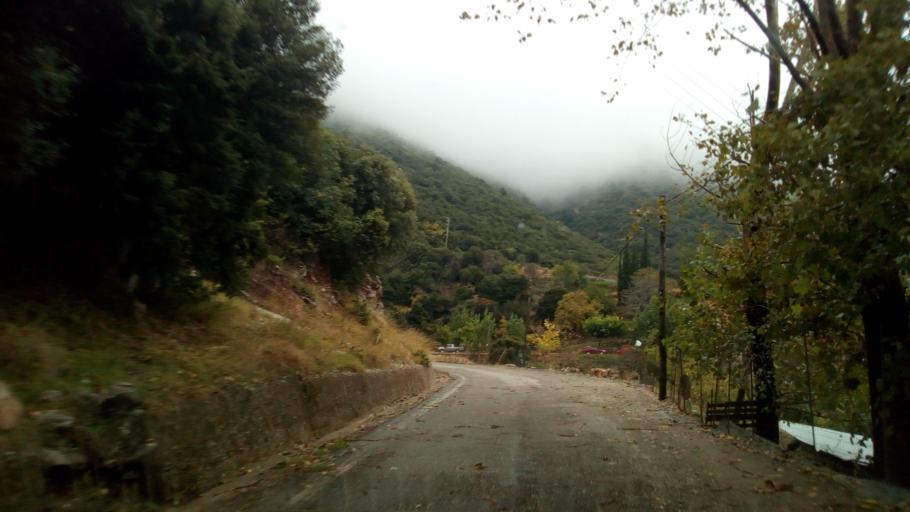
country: GR
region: West Greece
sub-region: Nomos Aitolias kai Akarnanias
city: Nafpaktos
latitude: 38.5209
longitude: 21.8422
